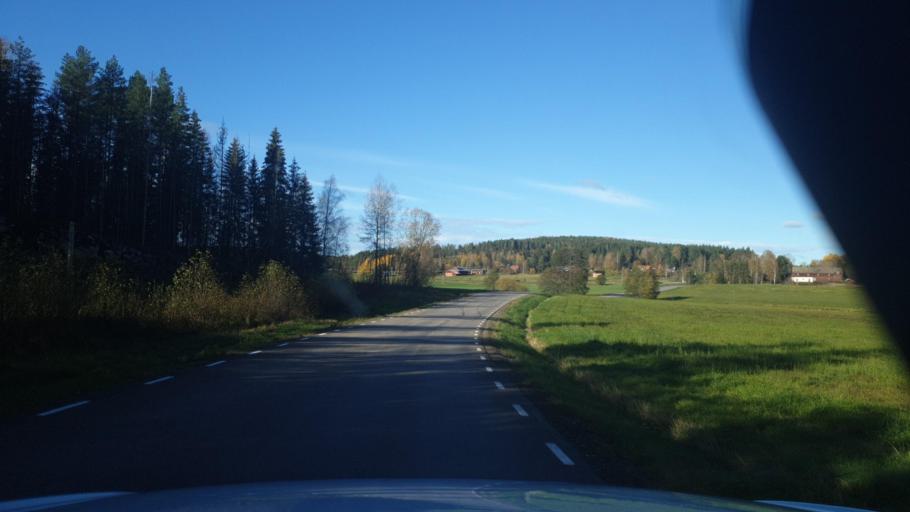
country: SE
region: Vaermland
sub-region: Arvika Kommun
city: Arvika
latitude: 59.6314
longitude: 12.7980
